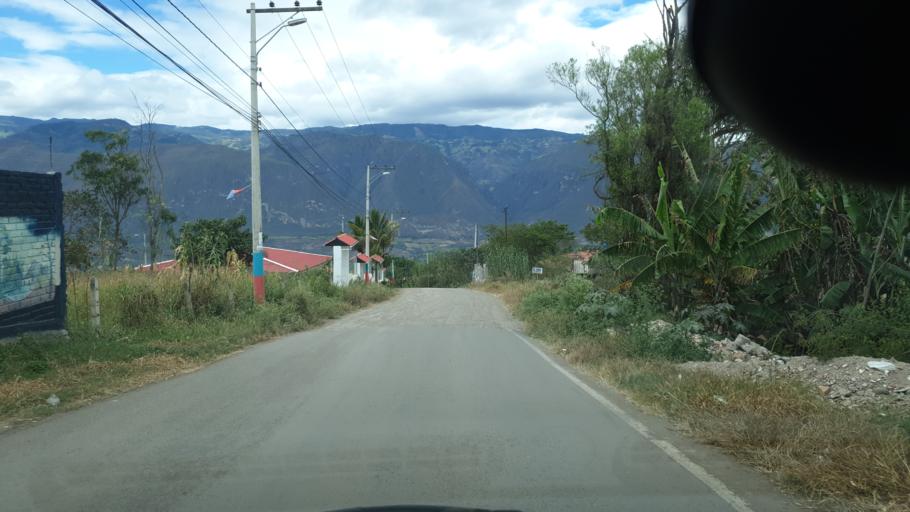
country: EC
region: Azuay
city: Cuenca
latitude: -3.2760
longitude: -79.3115
